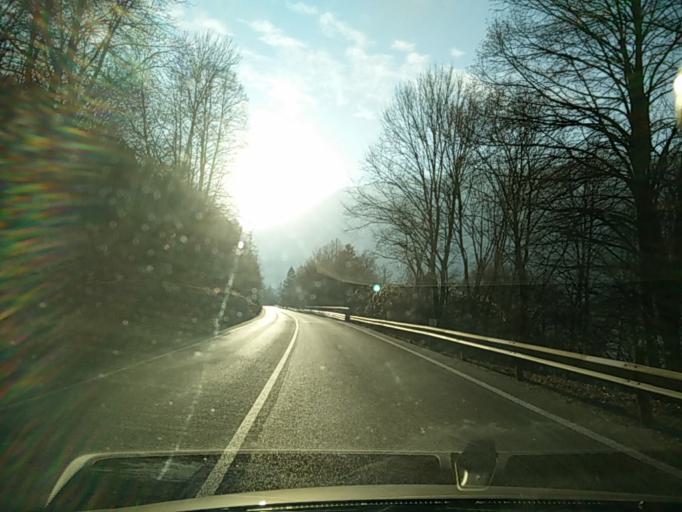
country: IT
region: Veneto
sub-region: Provincia di Belluno
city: Farra d'Alpago
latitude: 46.1037
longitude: 12.3516
